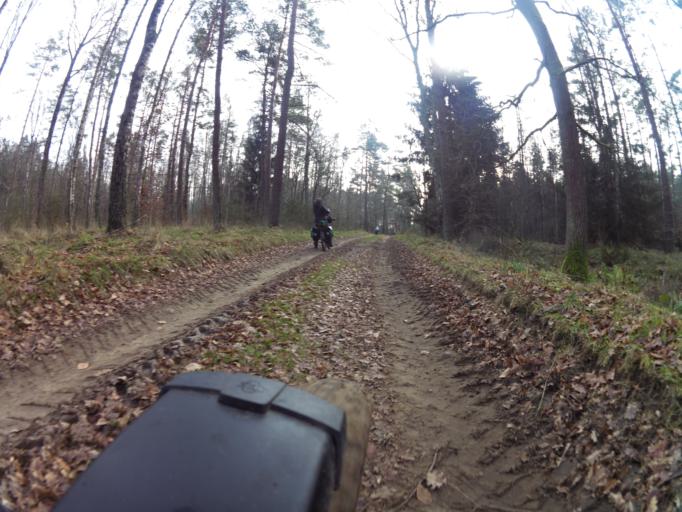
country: PL
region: West Pomeranian Voivodeship
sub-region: Powiat koszalinski
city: Polanow
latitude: 54.1492
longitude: 16.7304
